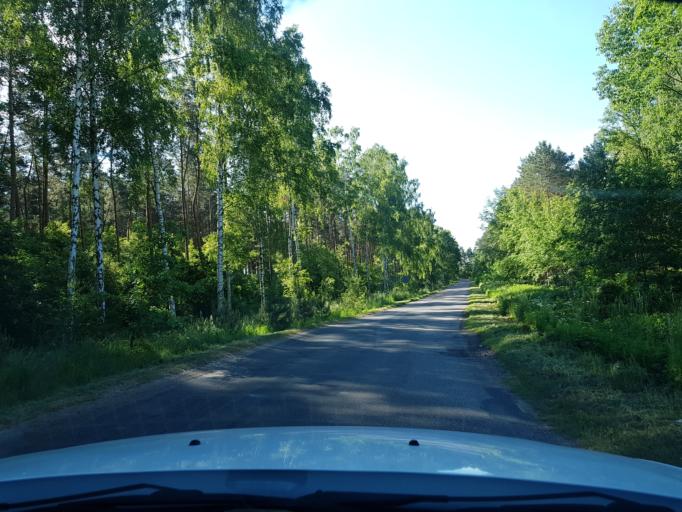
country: PL
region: West Pomeranian Voivodeship
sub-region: Powiat pyrzycki
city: Bielice
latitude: 53.2027
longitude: 14.6179
